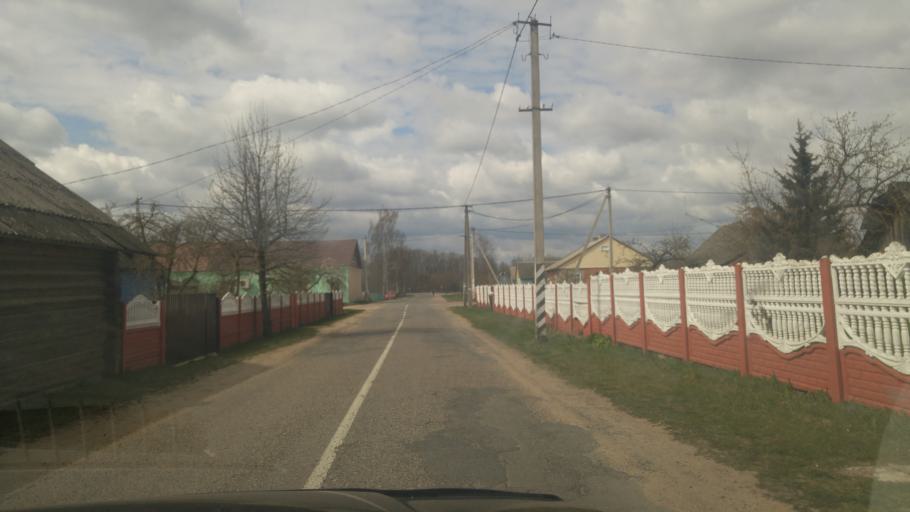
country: BY
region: Minsk
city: Pukhavichy
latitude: 53.4160
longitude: 28.2634
